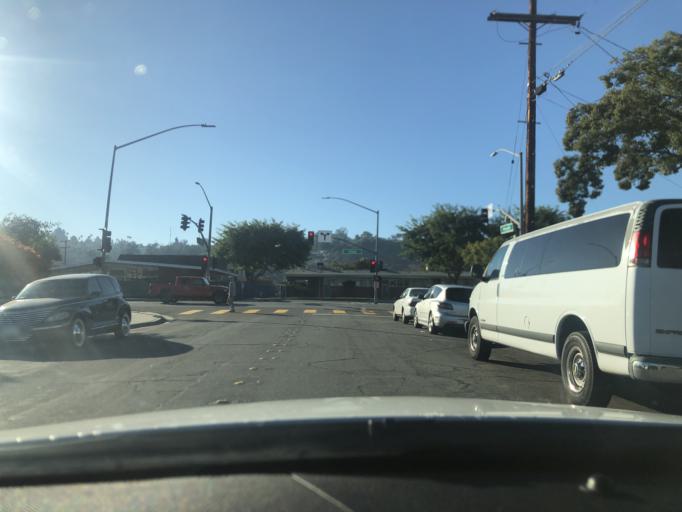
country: US
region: California
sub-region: San Diego County
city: El Cajon
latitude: 32.7809
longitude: -116.9600
